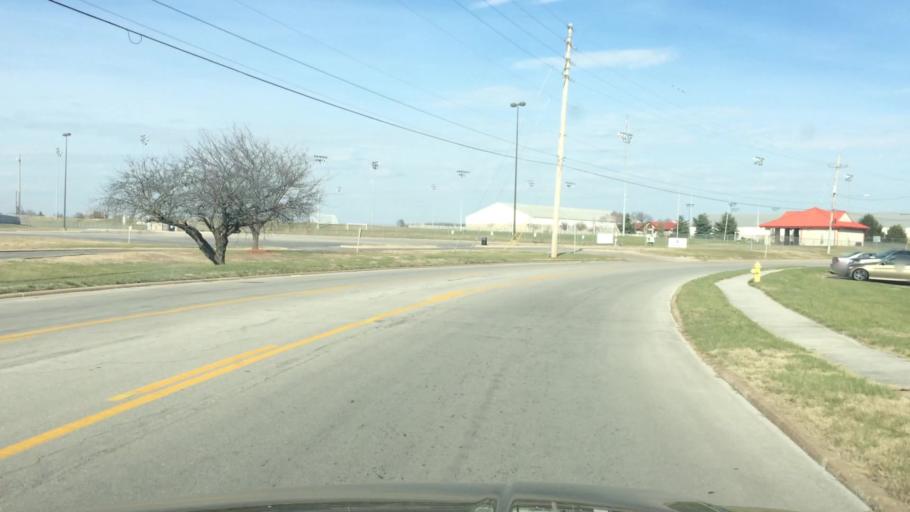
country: US
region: Missouri
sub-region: Greene County
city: Springfield
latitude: 37.2177
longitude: -93.2543
